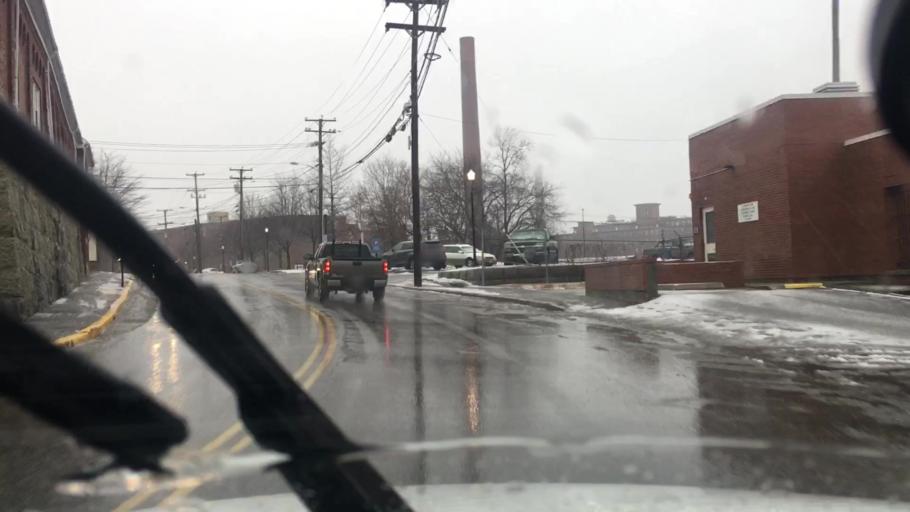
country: US
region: Maine
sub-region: York County
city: Biddeford
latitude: 43.4916
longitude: -70.4479
